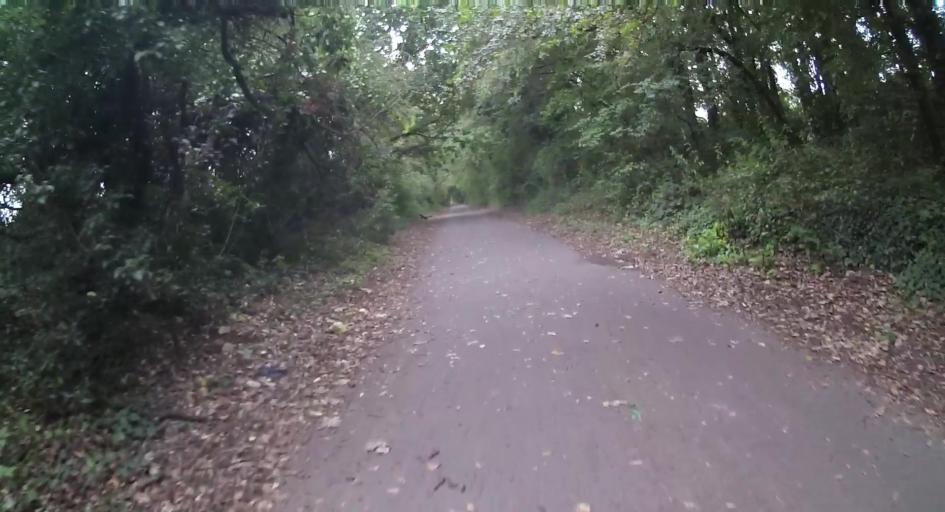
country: GB
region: England
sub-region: Isle of Wight
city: East Cowes
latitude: 50.7483
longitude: -1.2944
